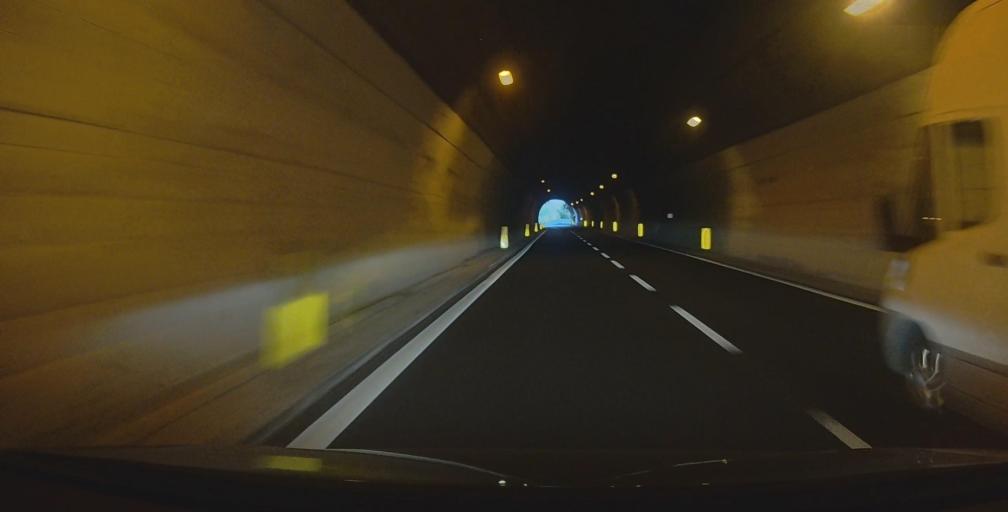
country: IT
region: Sicily
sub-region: Messina
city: Forza d'Agro
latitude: 37.9156
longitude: 15.3427
